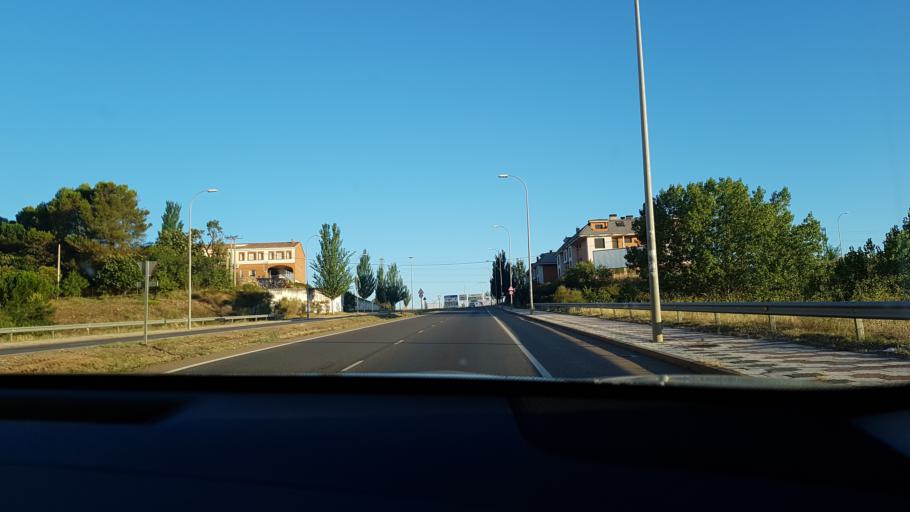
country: ES
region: Castille and Leon
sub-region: Provincia de Zamora
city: Zamora
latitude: 41.5175
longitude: -5.7481
